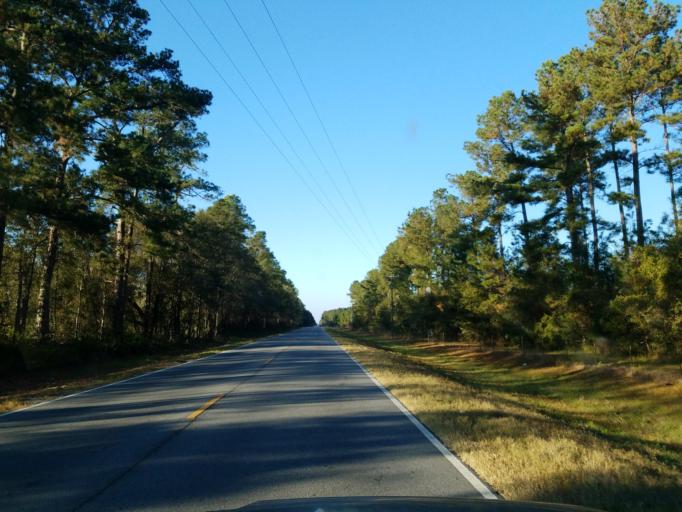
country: US
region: Georgia
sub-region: Lanier County
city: Lakeland
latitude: 31.0648
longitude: -83.0719
